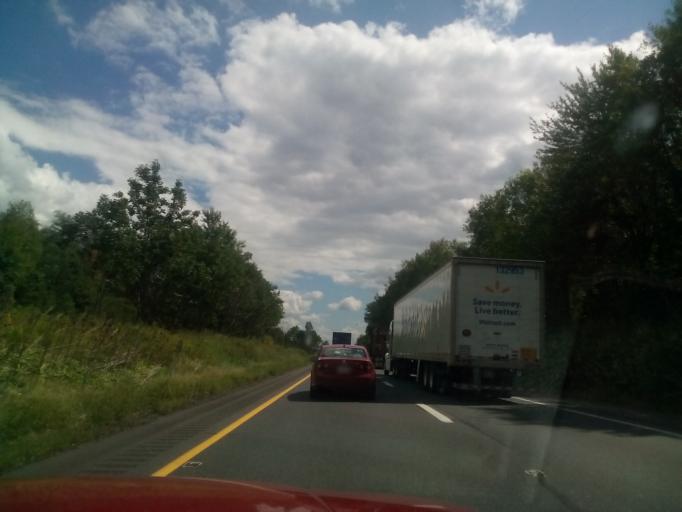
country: US
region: Pennsylvania
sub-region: Monroe County
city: Tannersville
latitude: 41.0305
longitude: -75.3096
